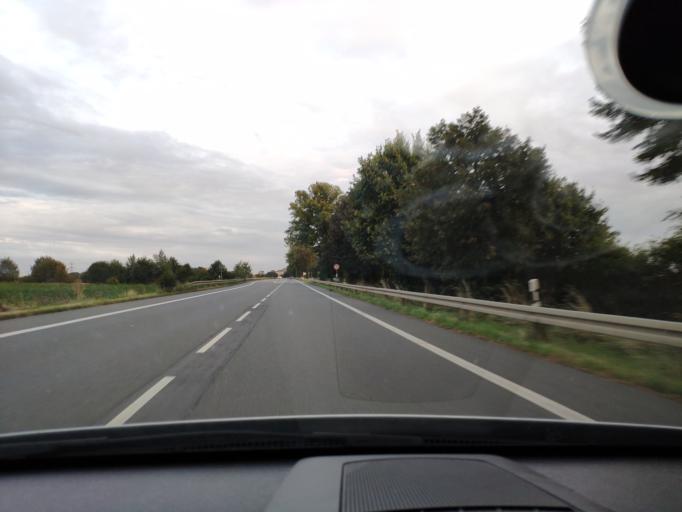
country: DE
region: North Rhine-Westphalia
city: Baesweiler
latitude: 50.9440
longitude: 6.1913
